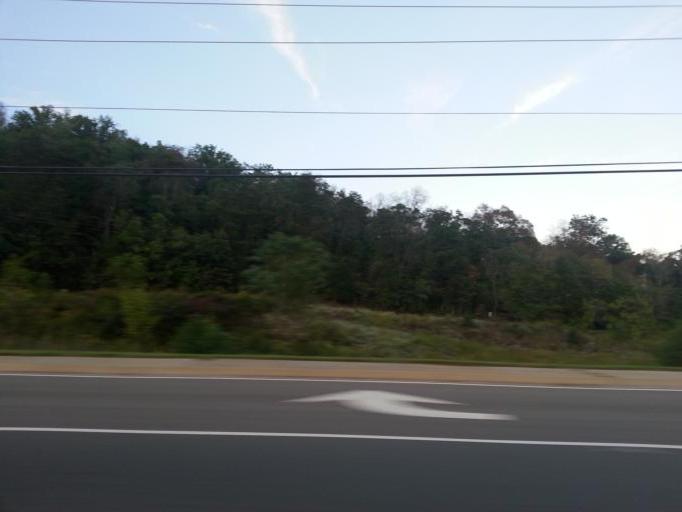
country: US
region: Tennessee
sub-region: Sevier County
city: Sevierville
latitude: 35.8866
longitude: -83.5737
